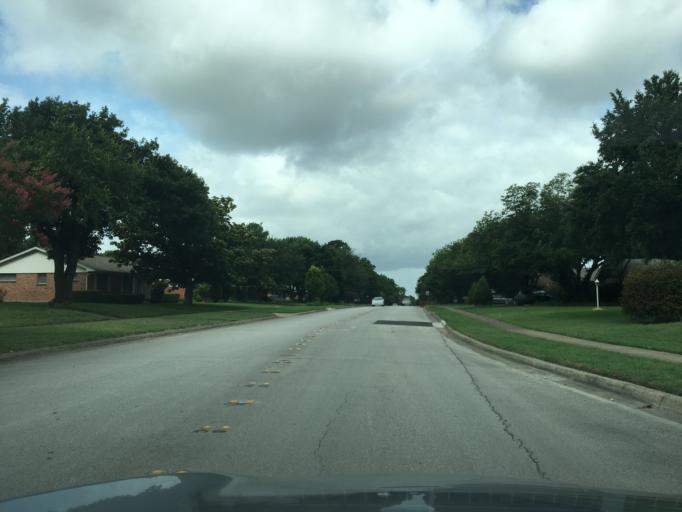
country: US
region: Texas
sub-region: Dallas County
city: Richardson
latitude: 32.9399
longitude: -96.7187
